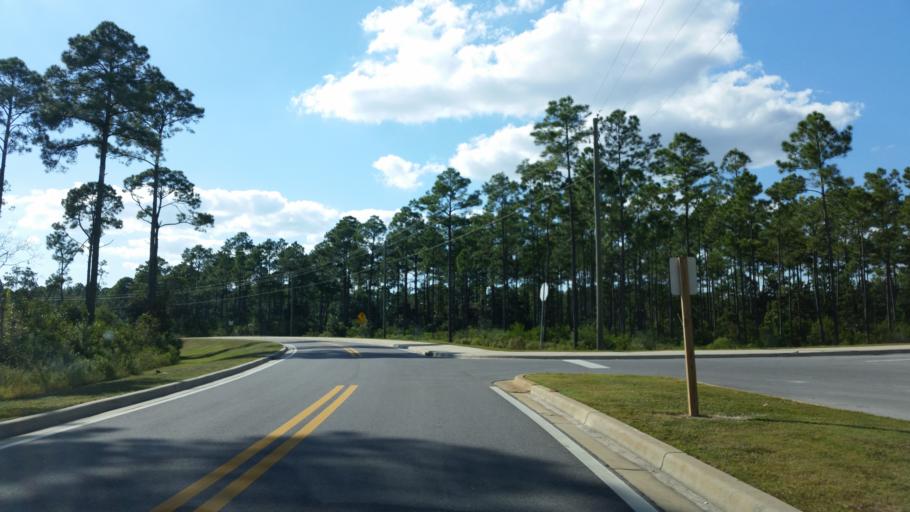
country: US
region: Florida
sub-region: Escambia County
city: Myrtle Grove
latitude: 30.3869
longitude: -87.3952
